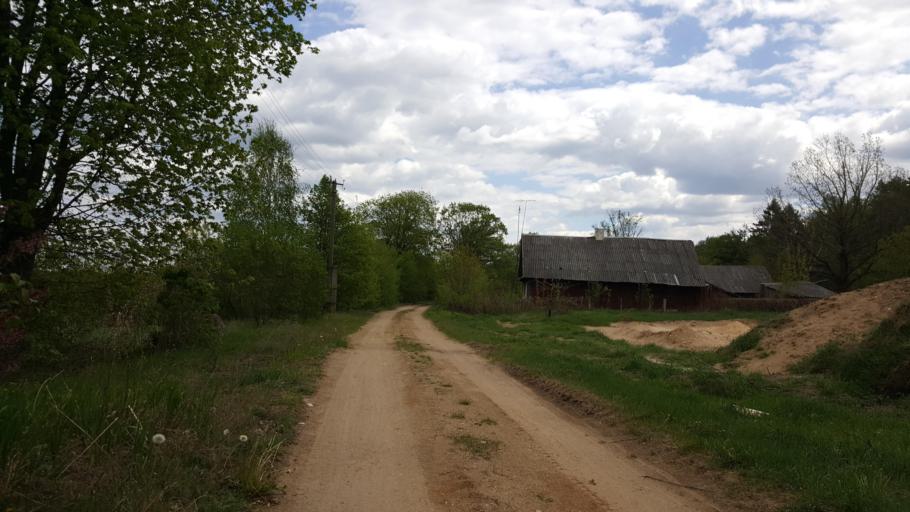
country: BY
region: Brest
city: Zhabinka
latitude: 52.3910
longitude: 24.0392
